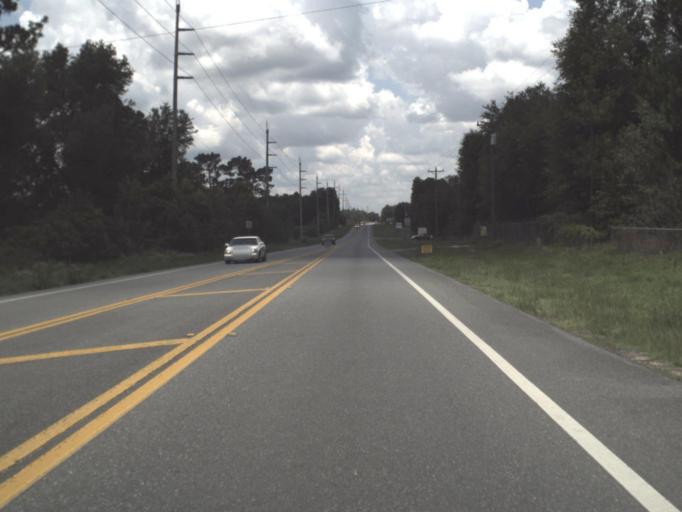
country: US
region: Florida
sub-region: Alachua County
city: Newberry
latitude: 29.6343
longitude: -82.6917
